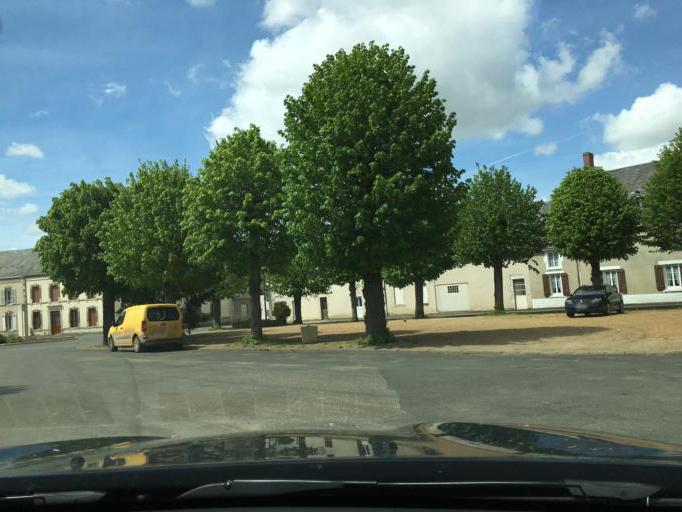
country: FR
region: Centre
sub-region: Departement du Loiret
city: Patay
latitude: 48.0827
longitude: 1.7413
